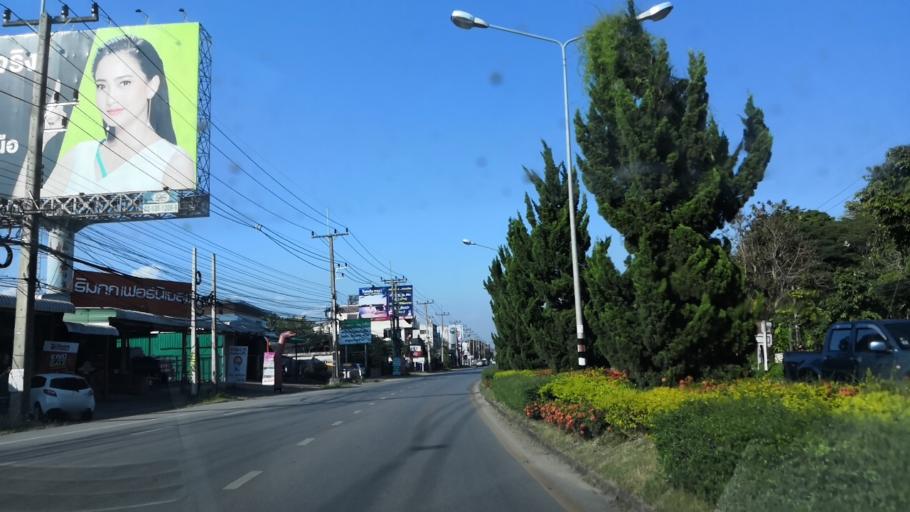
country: TH
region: Chiang Rai
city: Chiang Rai
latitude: 19.9268
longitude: 99.8442
